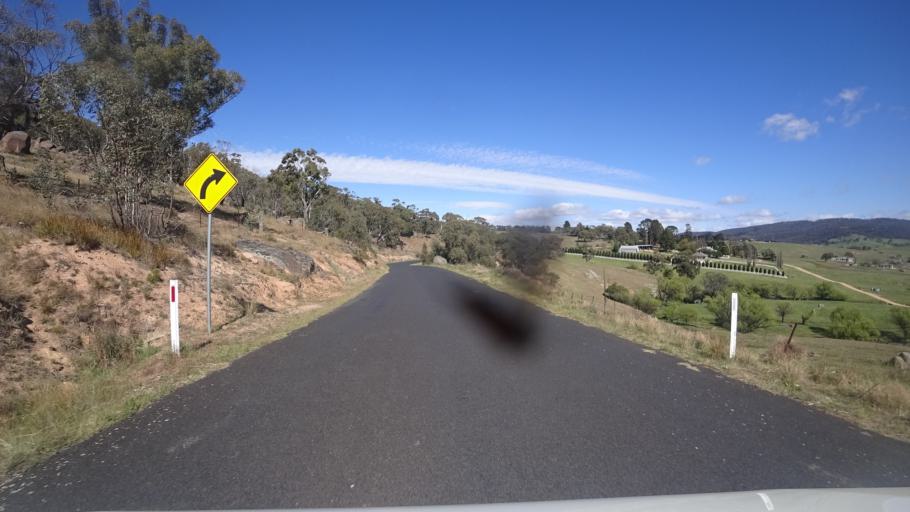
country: AU
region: New South Wales
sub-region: Lithgow
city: Bowenfels
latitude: -33.5167
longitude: 150.0015
